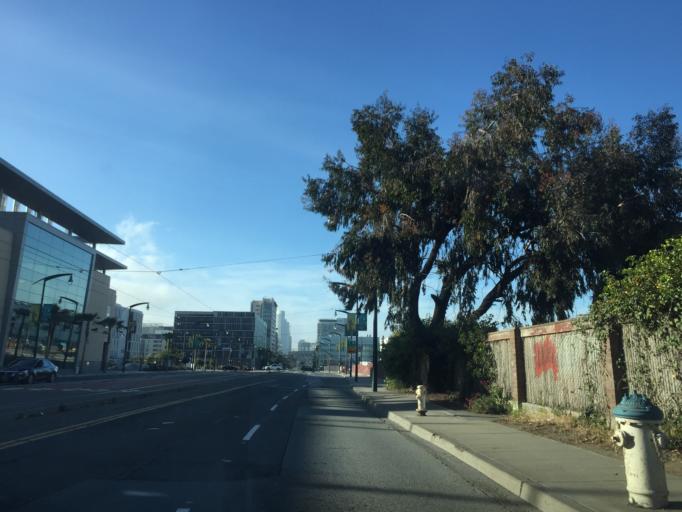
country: US
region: California
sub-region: San Francisco County
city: San Francisco
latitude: 37.7654
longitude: -122.3889
